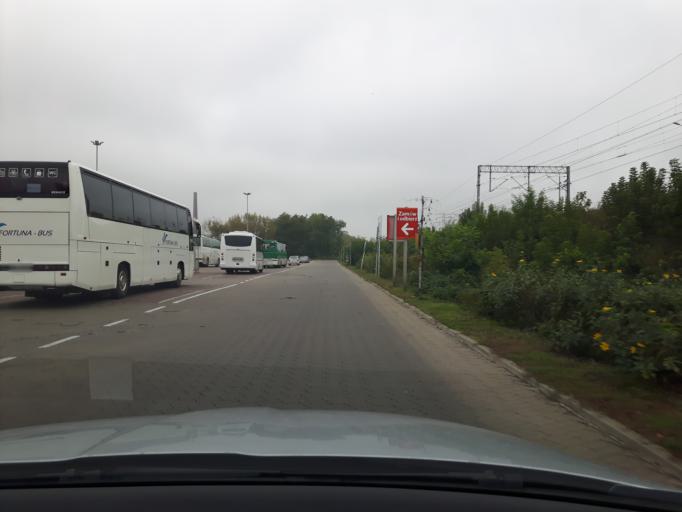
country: PL
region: Masovian Voivodeship
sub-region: Warszawa
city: Praga Polnoc
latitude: 52.2640
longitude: 21.0518
